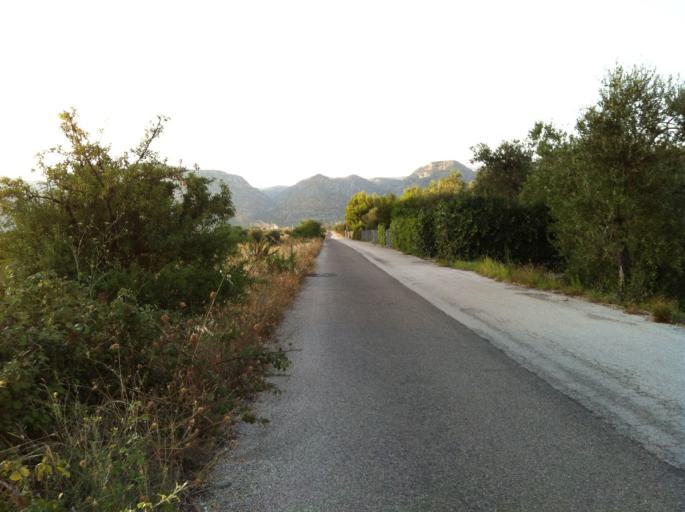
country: IT
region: Apulia
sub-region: Provincia di Foggia
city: Manfredonia
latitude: 41.6543
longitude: 15.9524
